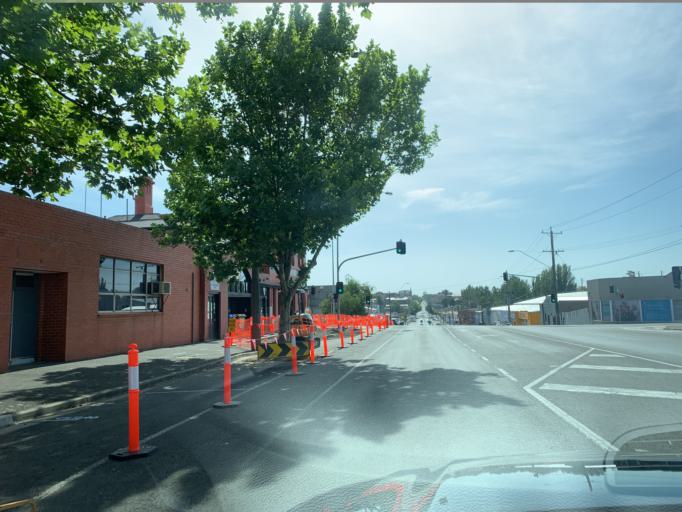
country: AU
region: Victoria
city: Ballarat East
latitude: -37.5609
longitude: 143.8670
